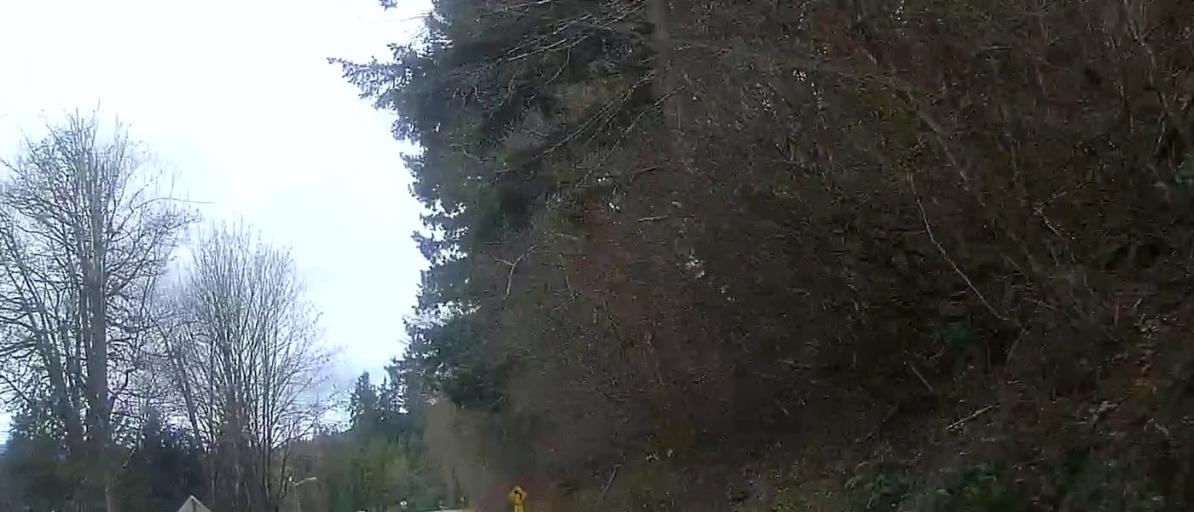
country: US
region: Washington
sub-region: Skagit County
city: Sedro-Woolley
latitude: 48.5815
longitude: -122.2543
